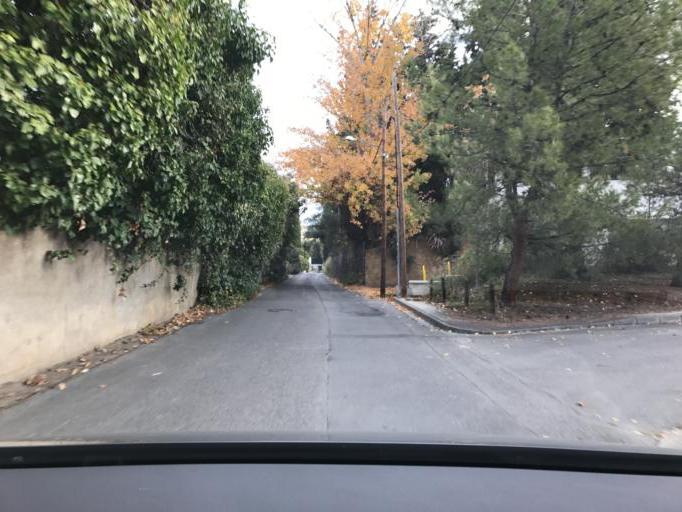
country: ES
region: Andalusia
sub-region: Provincia de Granada
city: Huetor Vega
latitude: 37.1524
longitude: -3.5803
